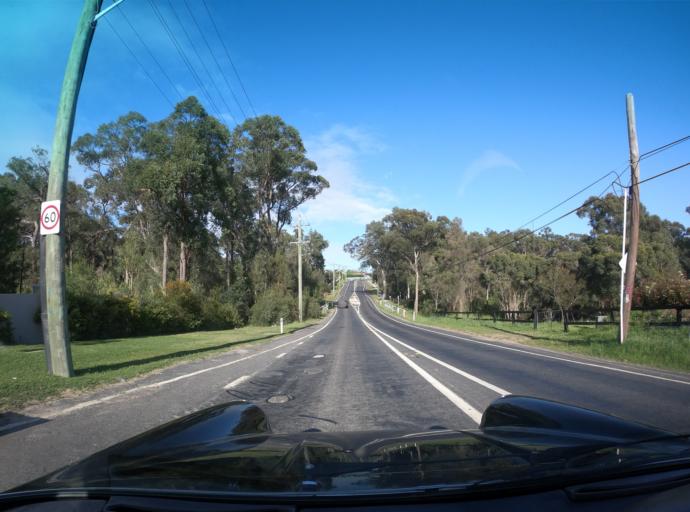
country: AU
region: New South Wales
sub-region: The Hills Shire
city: Beaumont Hills
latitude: -33.6877
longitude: 150.9444
